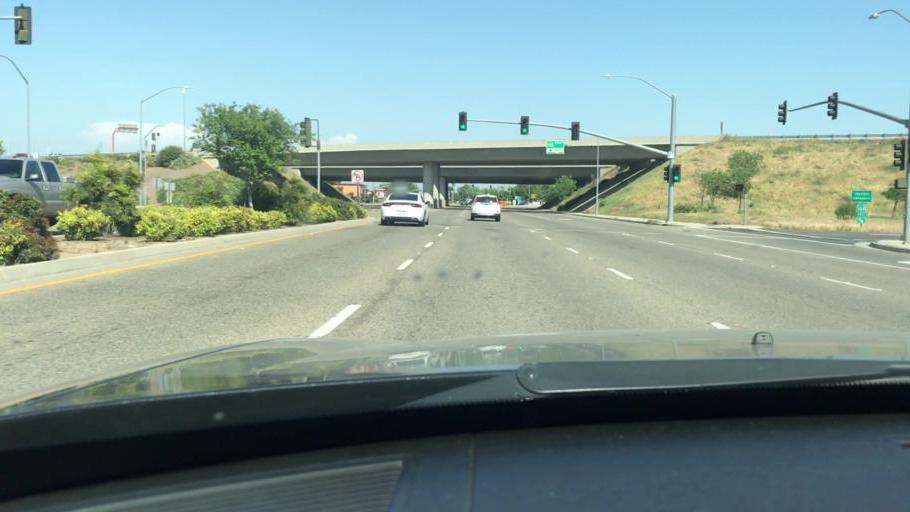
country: US
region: California
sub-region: Fresno County
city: Clovis
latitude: 36.8373
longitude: -119.7053
